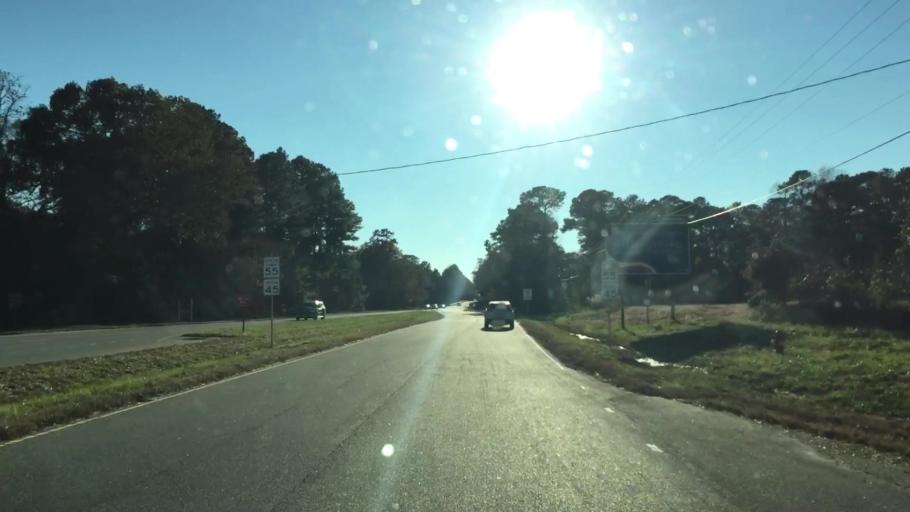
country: US
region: Virginia
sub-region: James City County
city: Williamsburg
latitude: 37.3803
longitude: -76.7685
